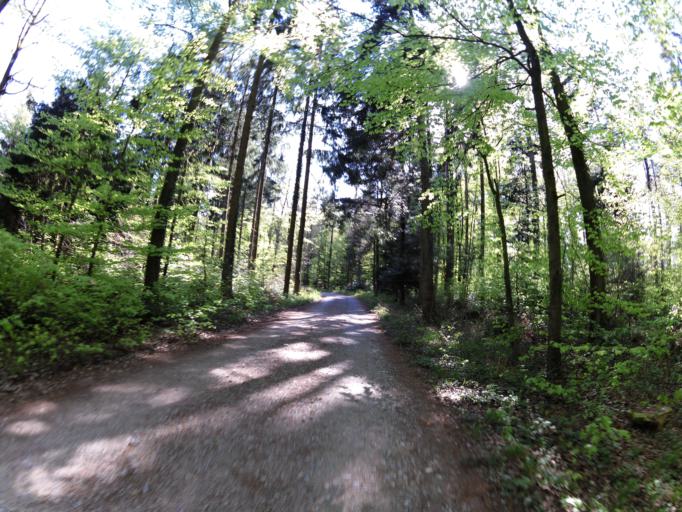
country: CH
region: Aargau
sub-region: Bezirk Aarau
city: Kuttigen
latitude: 47.4099
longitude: 8.0306
